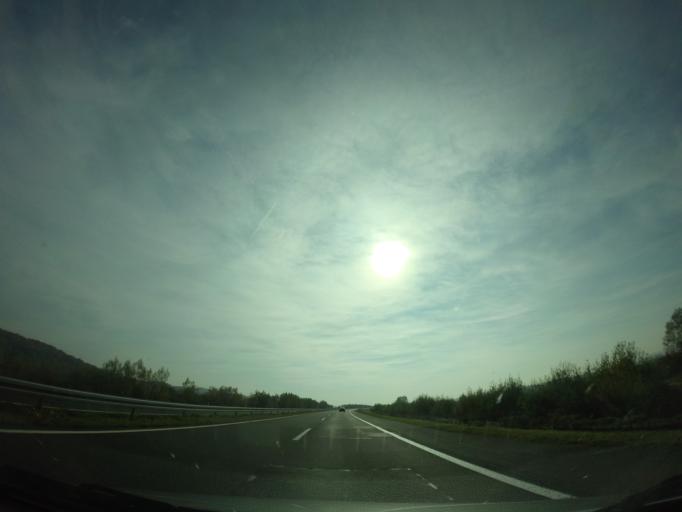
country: HR
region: Zagrebacka
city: Brckovljani
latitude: 46.0097
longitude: 16.2946
